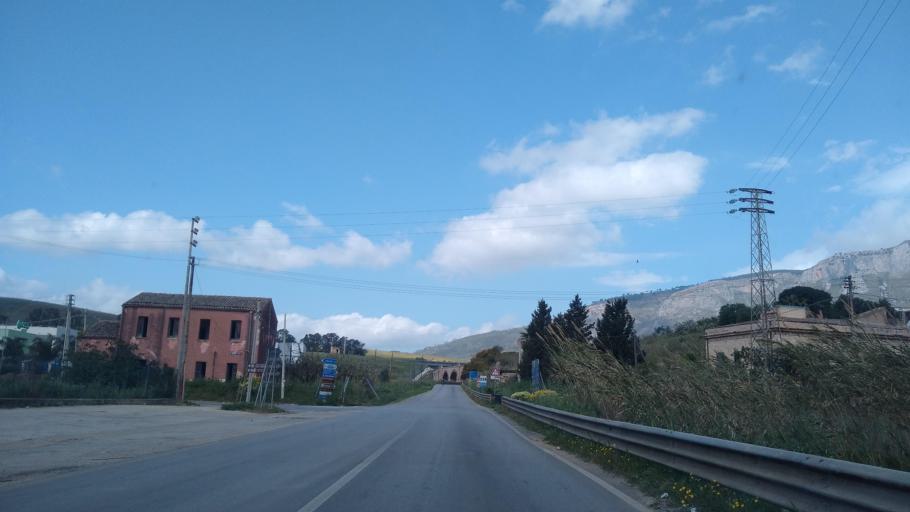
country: IT
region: Sicily
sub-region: Trapani
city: Alcamo
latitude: 37.9679
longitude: 12.9136
